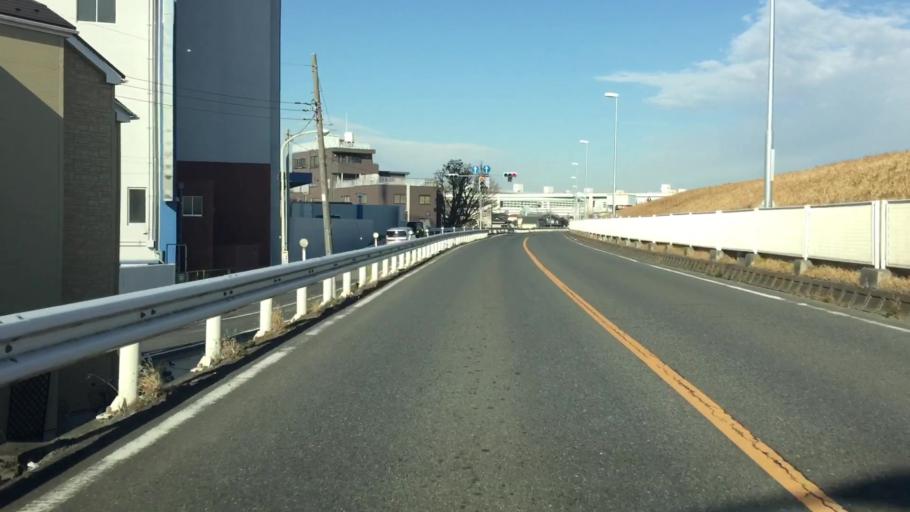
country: JP
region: Saitama
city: Kawaguchi
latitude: 35.7589
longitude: 139.7619
